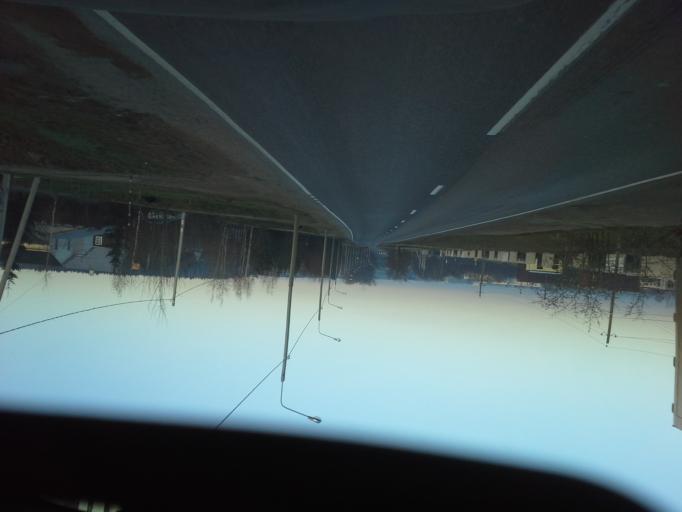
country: RU
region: Moskovskaya
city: Kokoshkino
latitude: 55.5794
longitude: 37.1516
